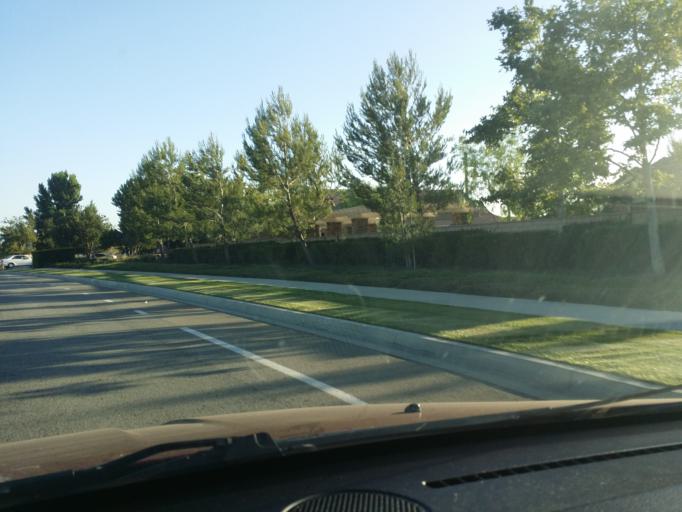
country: US
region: California
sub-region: San Bernardino County
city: Muscoy
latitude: 34.1931
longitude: -117.4179
